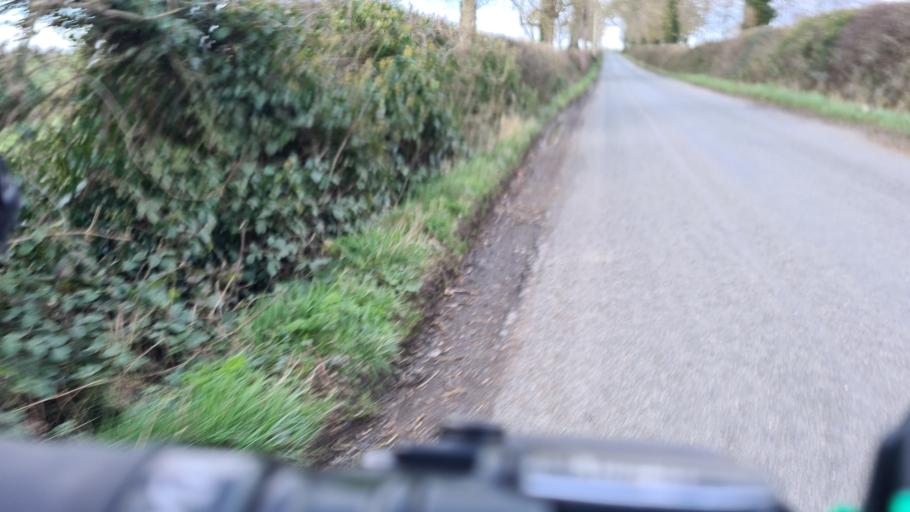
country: IE
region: Leinster
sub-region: Kildare
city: Celbridge
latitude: 53.3469
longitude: -6.5750
